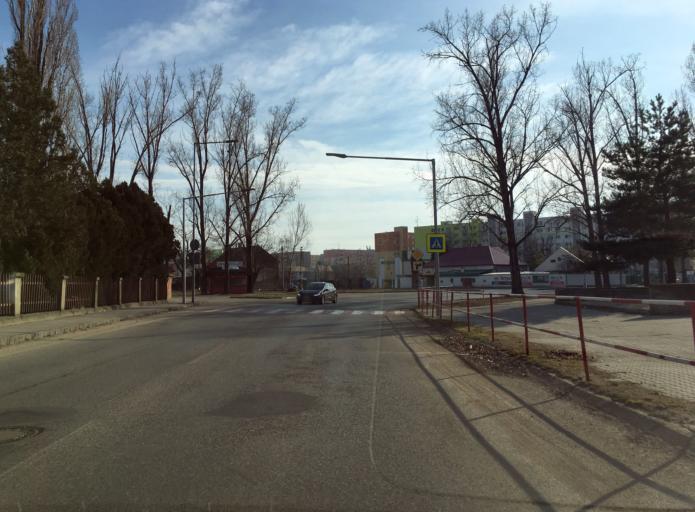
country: SK
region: Nitriansky
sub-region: Okres Nove Zamky
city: Nove Zamky
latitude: 47.9856
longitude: 18.1568
